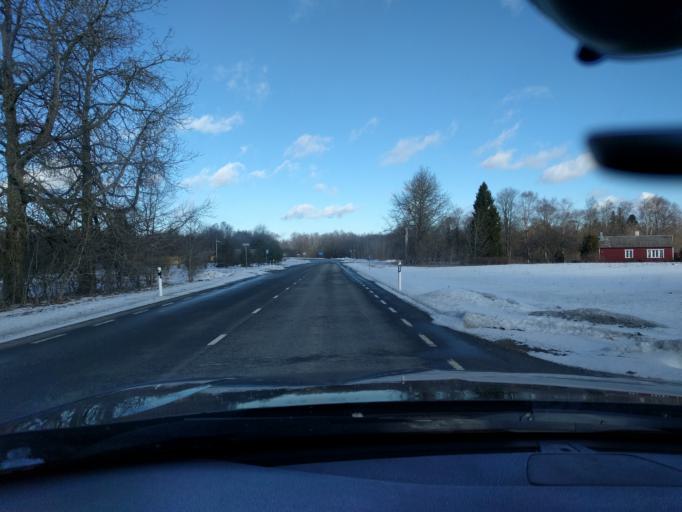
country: EE
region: Harju
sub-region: Raasiku vald
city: Raasiku
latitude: 59.3817
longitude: 25.1956
